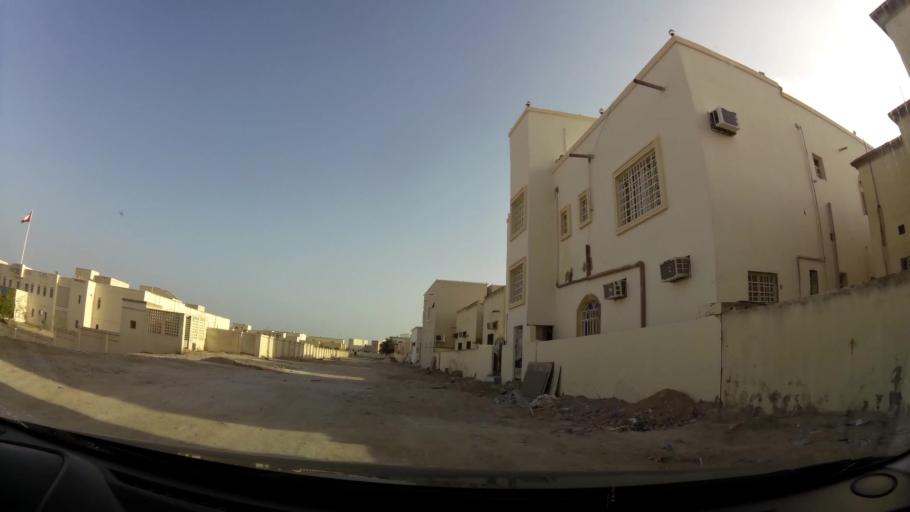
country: OM
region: Zufar
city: Salalah
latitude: 17.0108
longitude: 54.0319
